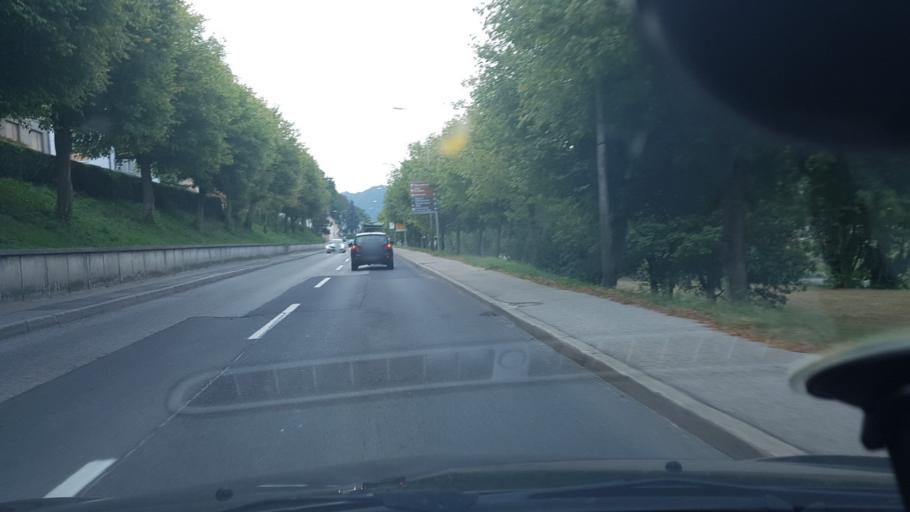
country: SI
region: Krsko
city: Krsko
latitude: 45.9542
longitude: 15.4865
